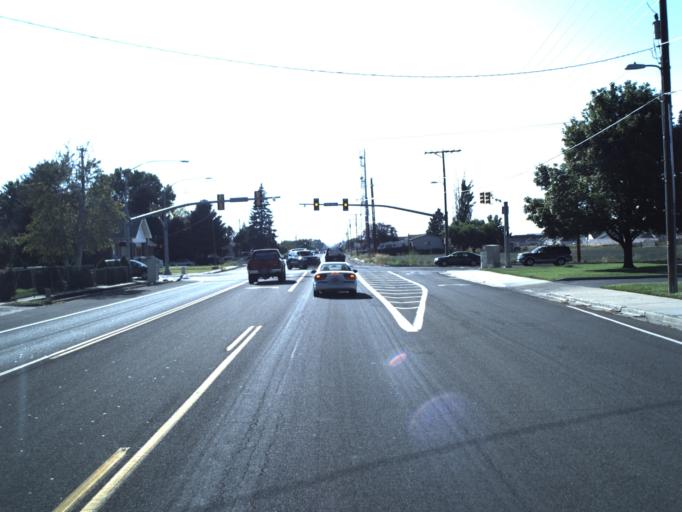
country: US
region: Utah
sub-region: Davis County
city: Clinton
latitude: 41.1399
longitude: -112.0538
